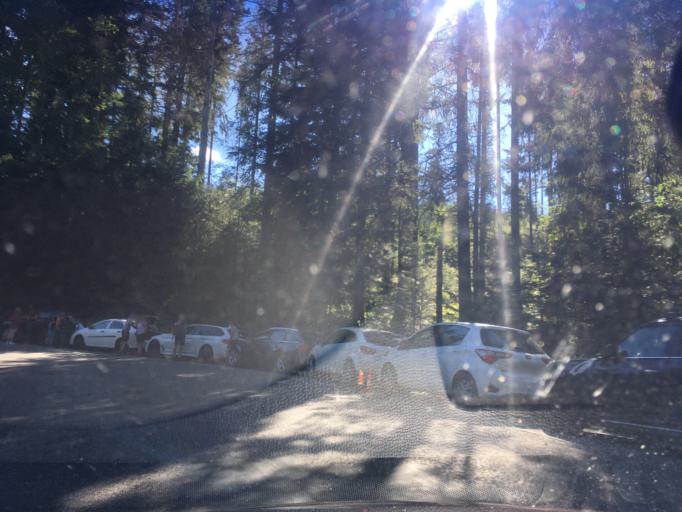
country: PL
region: Lesser Poland Voivodeship
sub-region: Powiat tatrzanski
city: Bukowina Tatrzanska
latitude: 49.2822
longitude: 20.0875
